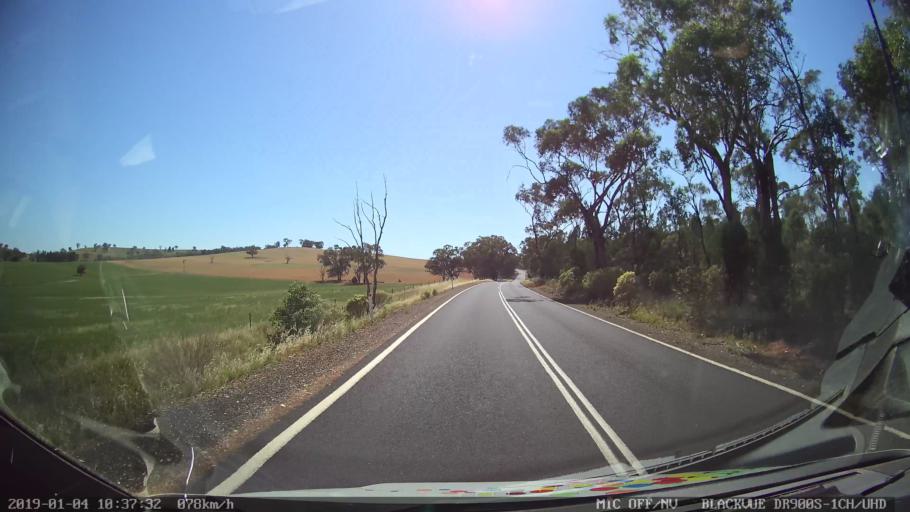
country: AU
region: New South Wales
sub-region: Cabonne
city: Molong
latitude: -33.2955
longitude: 148.6960
